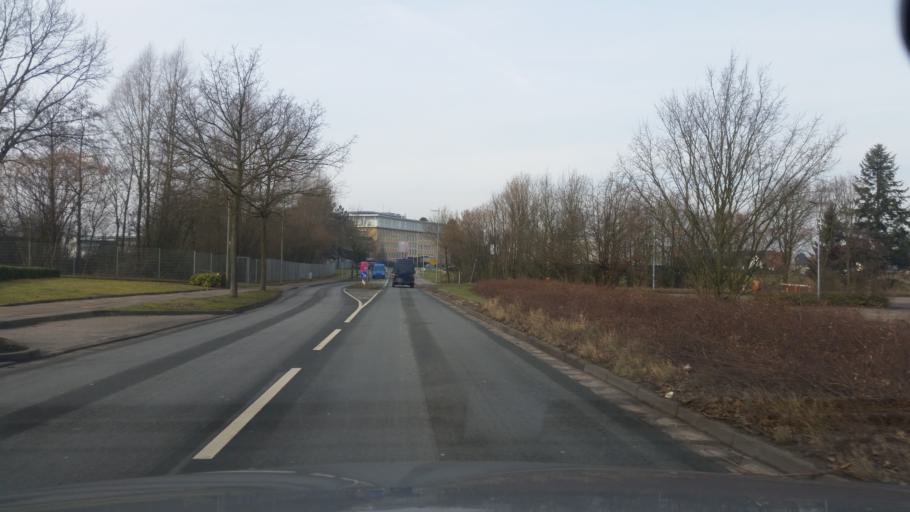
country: DE
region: North Rhine-Westphalia
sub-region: Regierungsbezirk Detmold
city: Bielefeld
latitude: 52.0086
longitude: 8.6029
